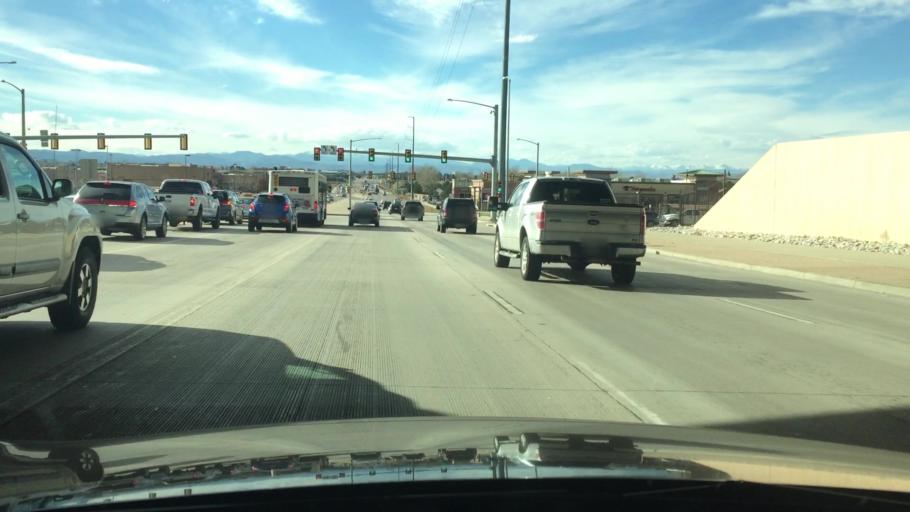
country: US
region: Colorado
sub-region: Arapahoe County
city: Dove Valley
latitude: 39.5951
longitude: -104.8024
